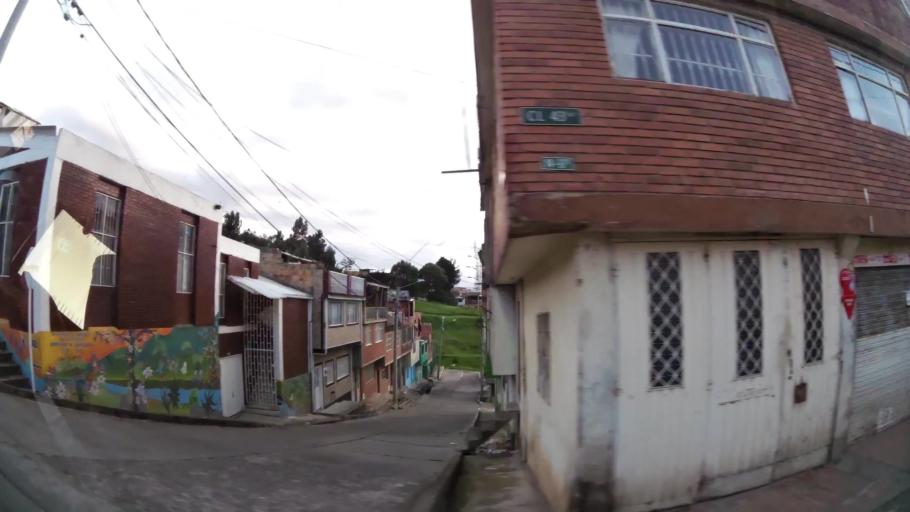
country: CO
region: Bogota D.C.
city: Bogota
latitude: 4.5435
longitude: -74.0824
